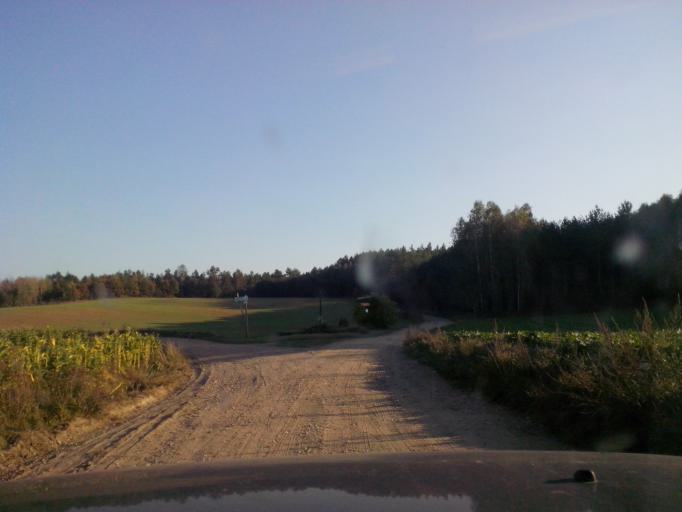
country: PL
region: Kujawsko-Pomorskie
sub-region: Powiat brodnicki
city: Gorzno
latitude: 53.2788
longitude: 19.7027
